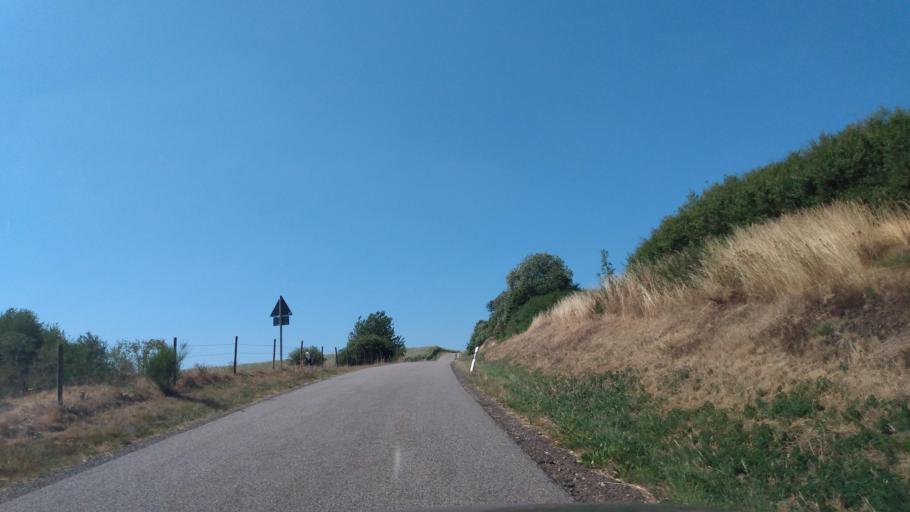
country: DE
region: Rheinland-Pfalz
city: Morbach
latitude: 49.8373
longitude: 7.1625
